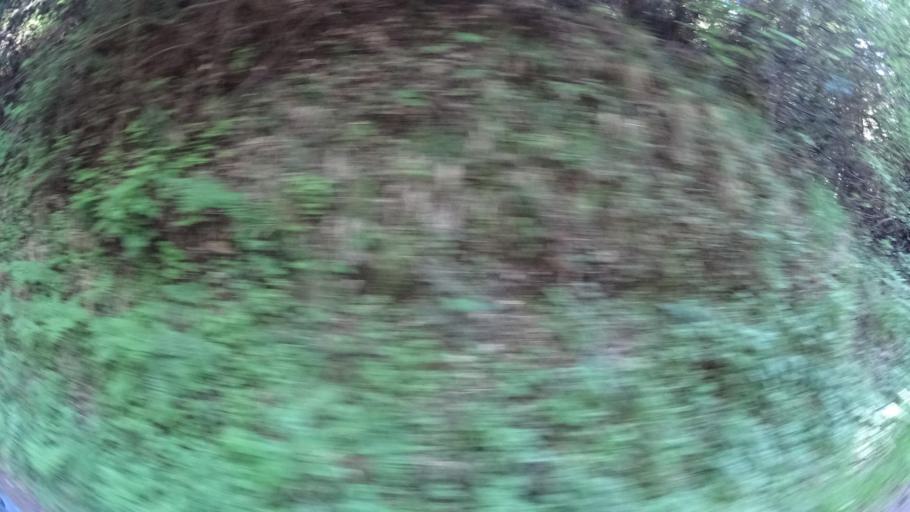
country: US
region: California
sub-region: Humboldt County
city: Rio Dell
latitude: 40.4580
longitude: -124.0384
